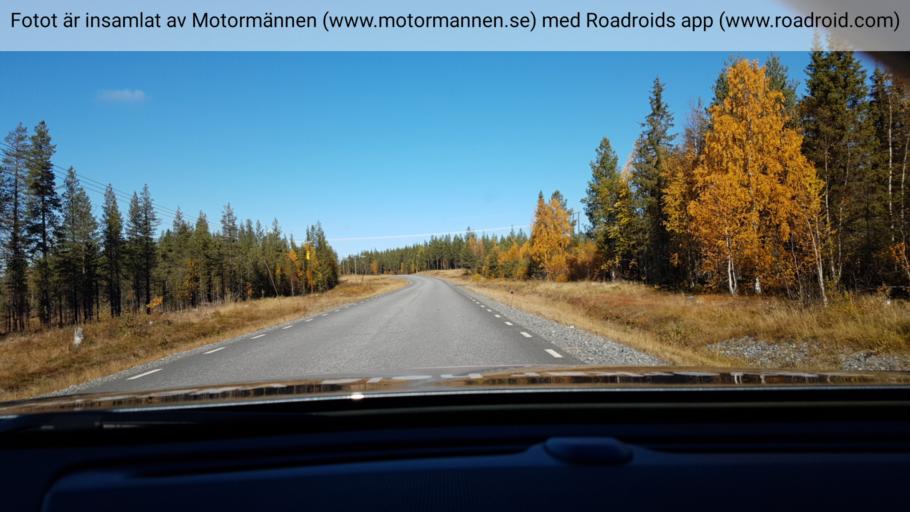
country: SE
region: Norrbotten
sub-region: Gallivare Kommun
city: Gaellivare
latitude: 66.8208
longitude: 21.0429
